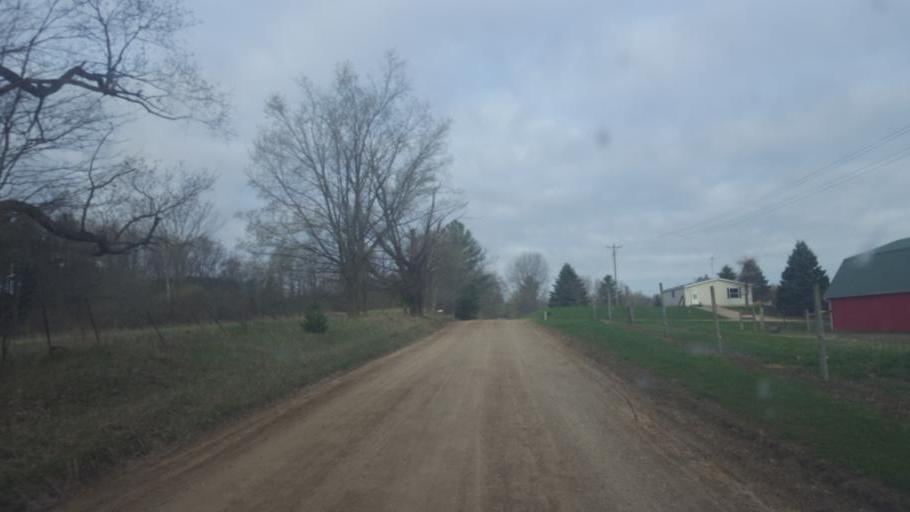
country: US
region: Michigan
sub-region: Isabella County
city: Lake Isabella
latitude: 43.5381
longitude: -85.0413
